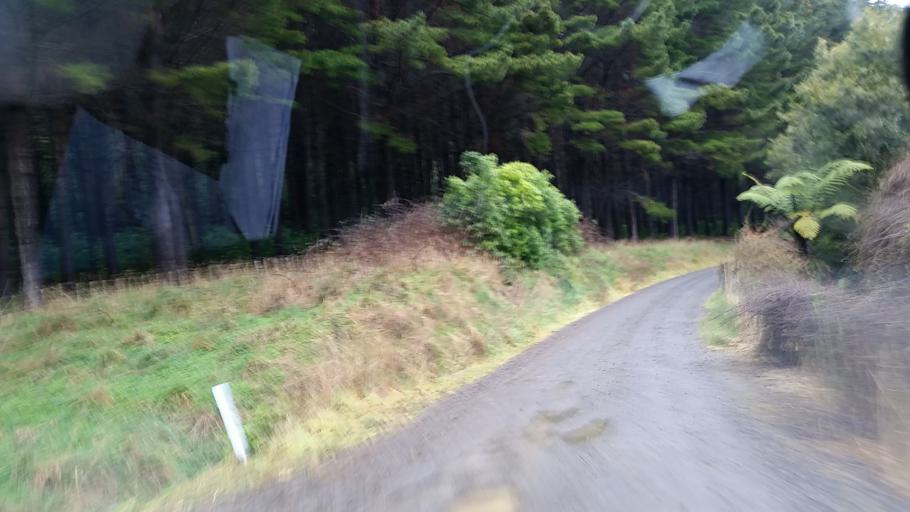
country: NZ
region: Taranaki
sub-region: South Taranaki District
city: Eltham
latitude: -39.5028
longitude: 174.4299
